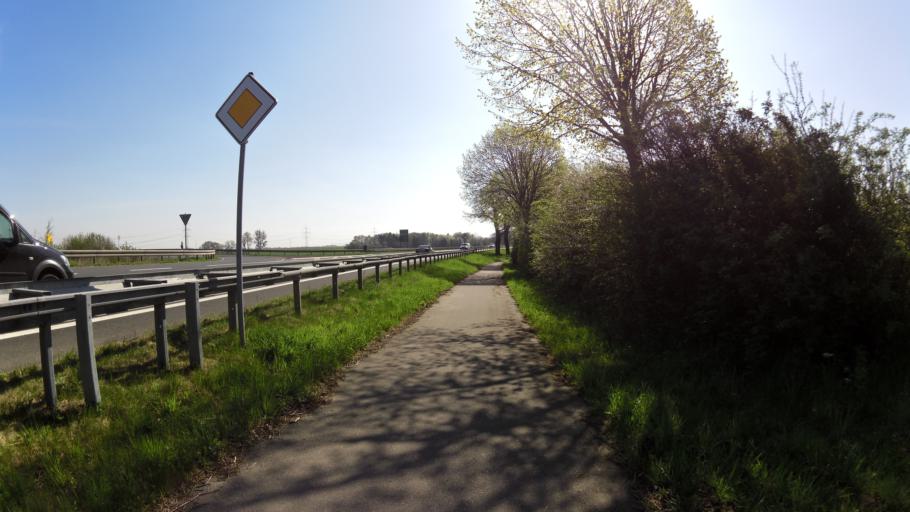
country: DE
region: North Rhine-Westphalia
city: Baesweiler
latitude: 50.9478
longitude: 6.1811
